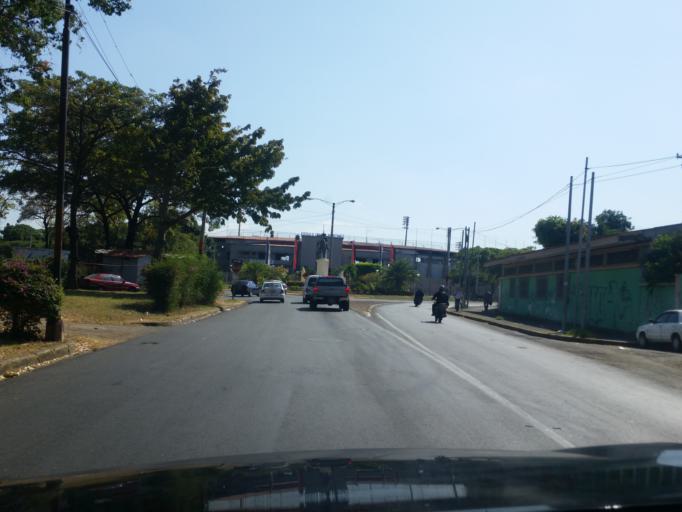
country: NI
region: Managua
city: Managua
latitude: 12.1519
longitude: -86.2826
